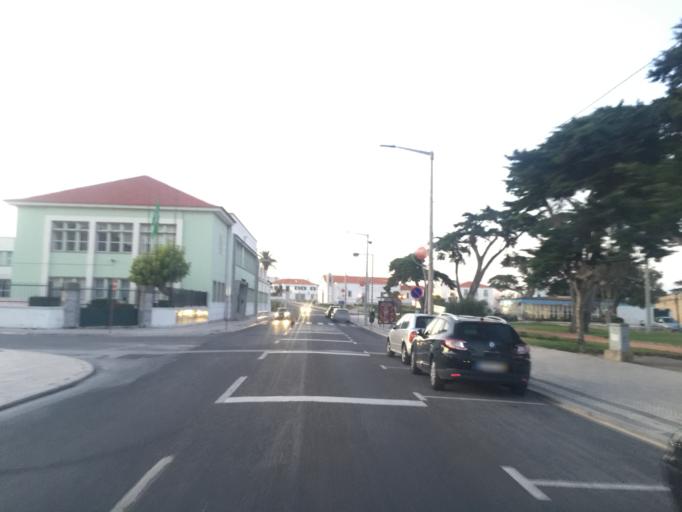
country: PT
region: Leiria
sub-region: Peniche
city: Peniche
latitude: 39.3632
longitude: -9.3789
